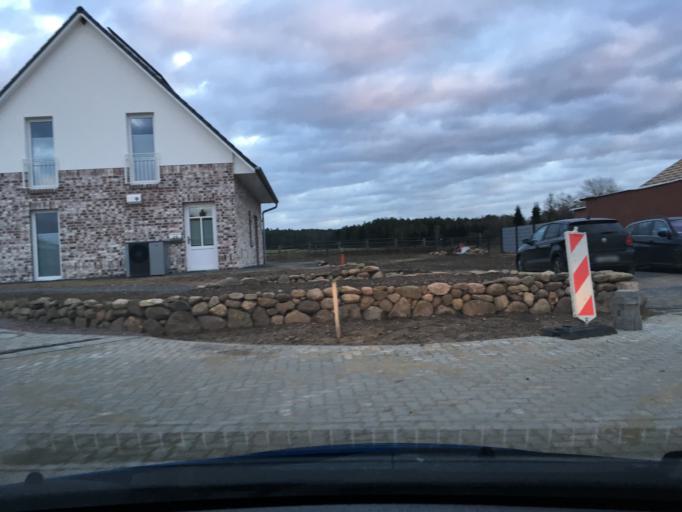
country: DE
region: Lower Saxony
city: Soderstorf
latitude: 53.1446
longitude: 10.1560
